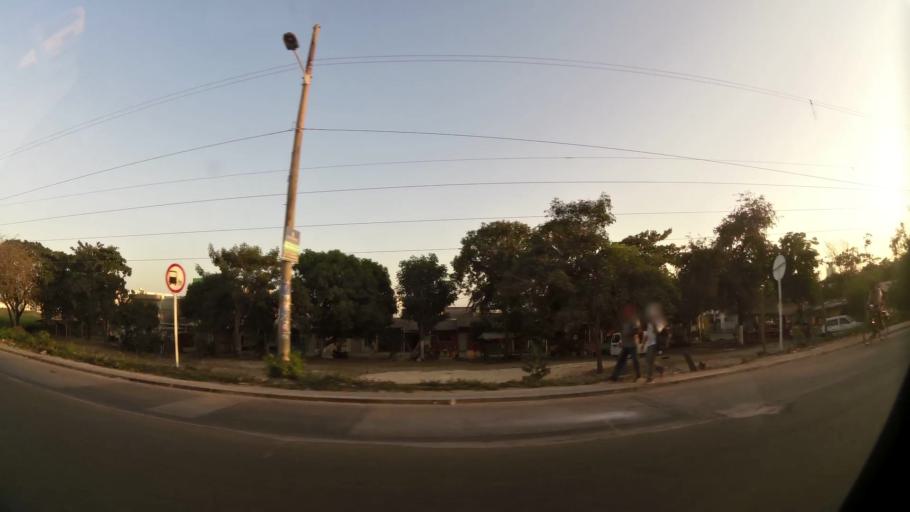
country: CO
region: Bolivar
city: Cartagena
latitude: 10.3986
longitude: -75.4704
